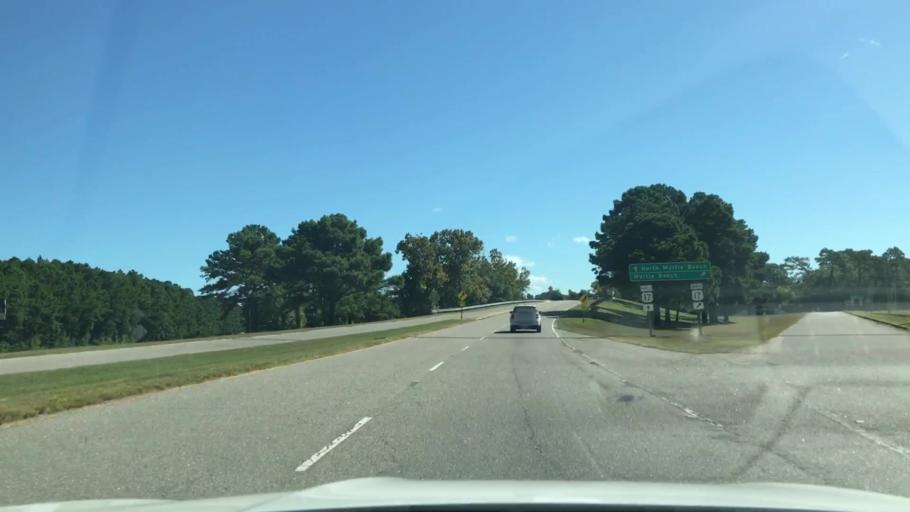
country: US
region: South Carolina
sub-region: Horry County
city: Myrtle Beach
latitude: 33.7662
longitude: -78.8080
